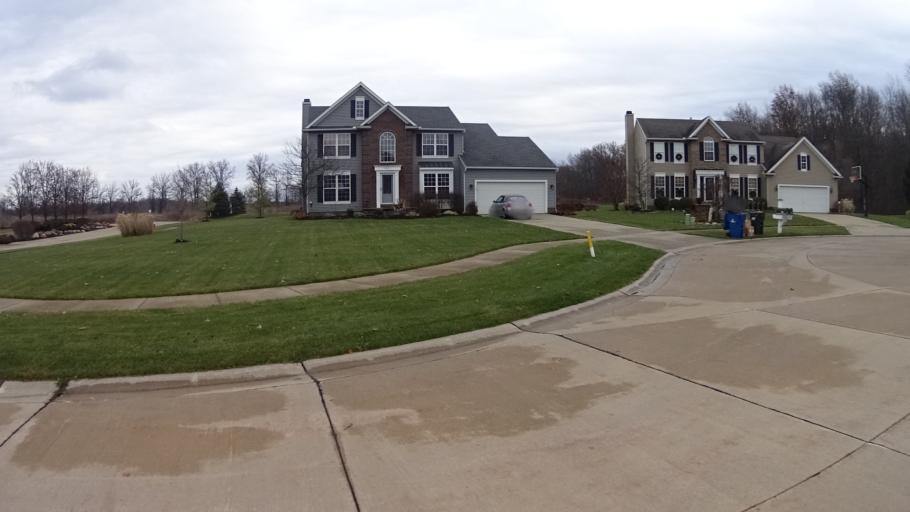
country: US
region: Ohio
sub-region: Lorain County
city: North Ridgeville
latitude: 41.3634
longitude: -82.0374
